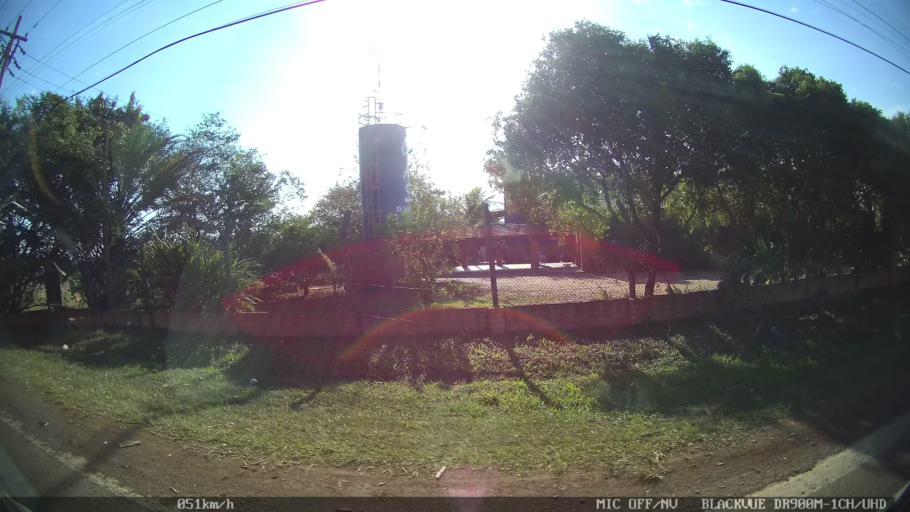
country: BR
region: Sao Paulo
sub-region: Piracicaba
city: Piracicaba
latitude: -22.6645
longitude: -47.6190
